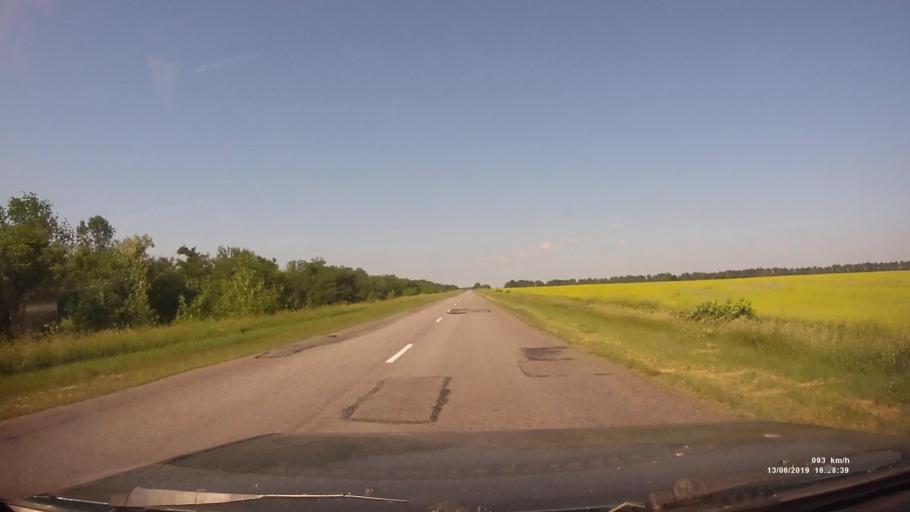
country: RU
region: Rostov
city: Kazanskaya
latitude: 49.8234
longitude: 41.2038
